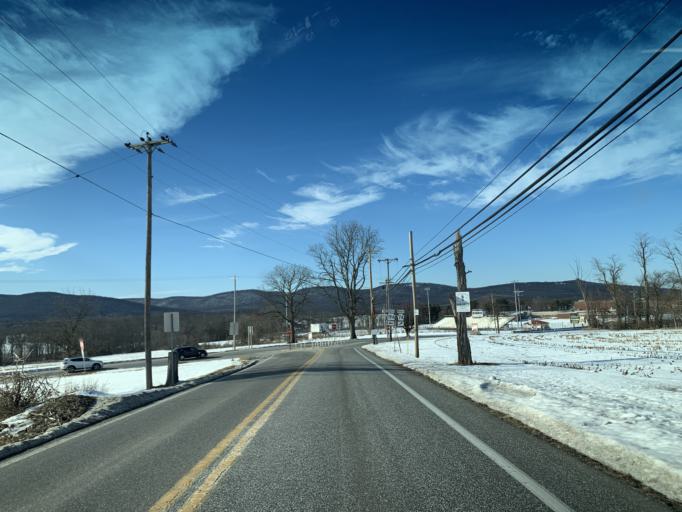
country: US
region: Pennsylvania
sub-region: York County
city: Dillsburg
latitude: 40.0926
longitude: -77.0302
